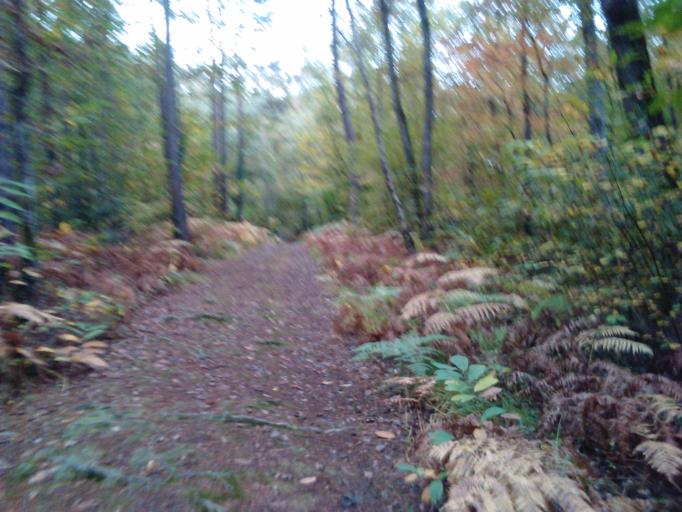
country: FR
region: Centre
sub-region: Departement du Loir-et-Cher
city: Naveil
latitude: 47.8182
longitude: 1.0395
